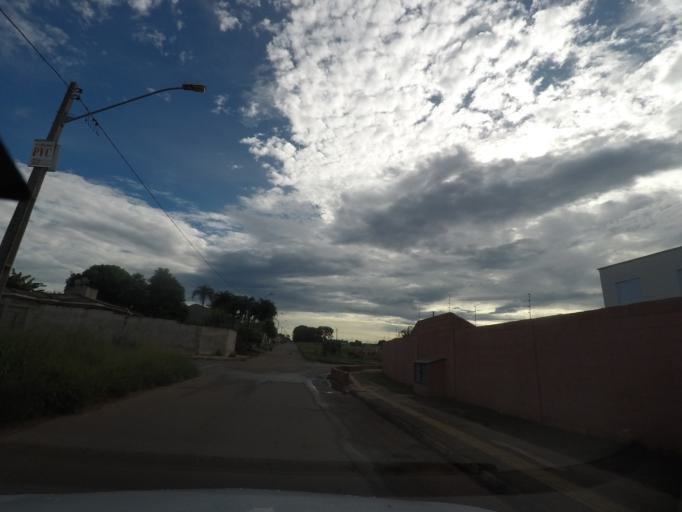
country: BR
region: Goias
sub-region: Aparecida De Goiania
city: Aparecida de Goiania
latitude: -16.7903
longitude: -49.3689
